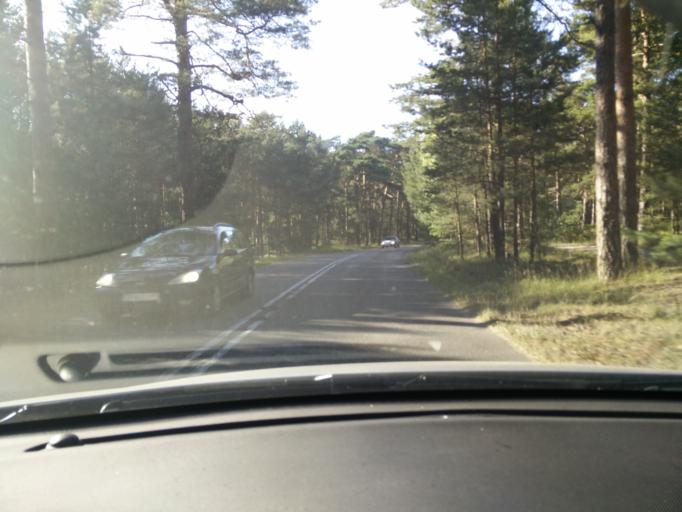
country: PL
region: Pomeranian Voivodeship
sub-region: Powiat pucki
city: Hel
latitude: 54.6443
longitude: 18.7704
